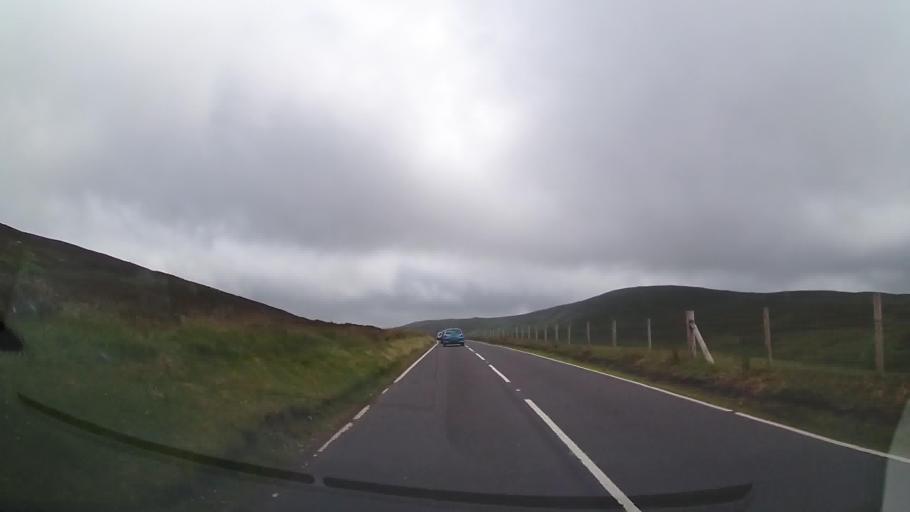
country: GB
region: Wales
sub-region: Denbighshire
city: Llandrillo
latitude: 52.8911
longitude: -3.4858
